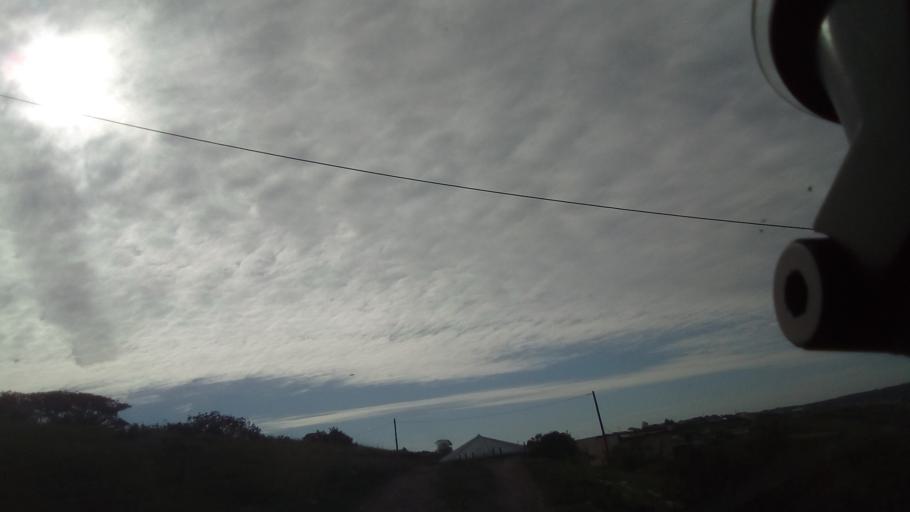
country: ZA
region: Eastern Cape
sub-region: Buffalo City Metropolitan Municipality
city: East London
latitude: -32.7962
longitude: 27.9566
